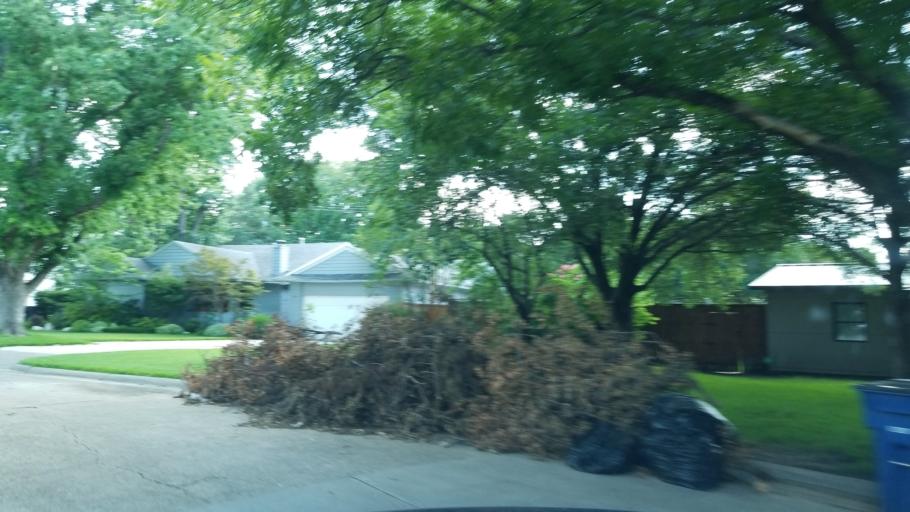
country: US
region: Texas
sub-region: Dallas County
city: University Park
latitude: 32.8892
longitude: -96.8428
